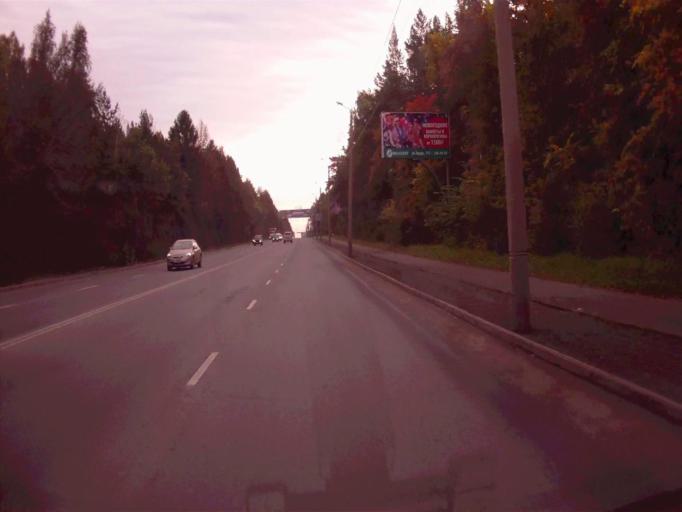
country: RU
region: Chelyabinsk
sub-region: Gorod Chelyabinsk
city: Chelyabinsk
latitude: 55.1469
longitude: 61.3456
